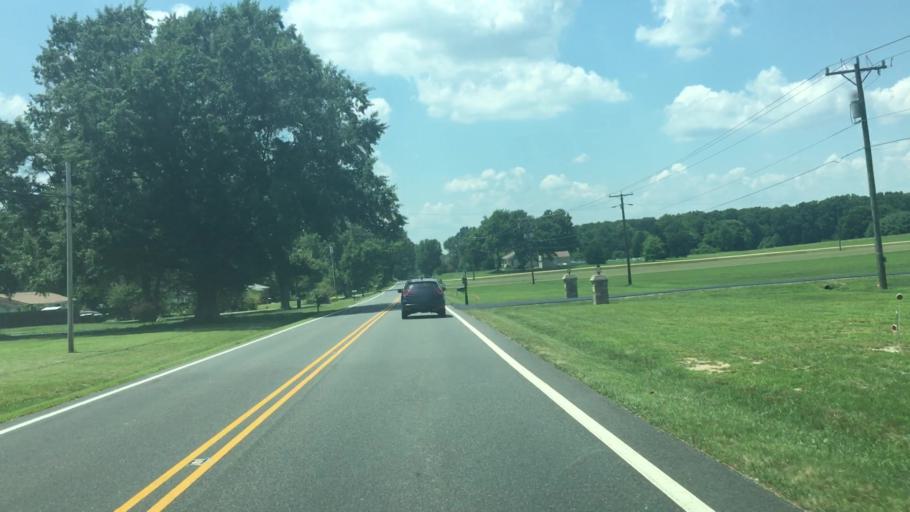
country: US
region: Virginia
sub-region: King George County
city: Passapatanzy
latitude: 38.3013
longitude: -77.3782
